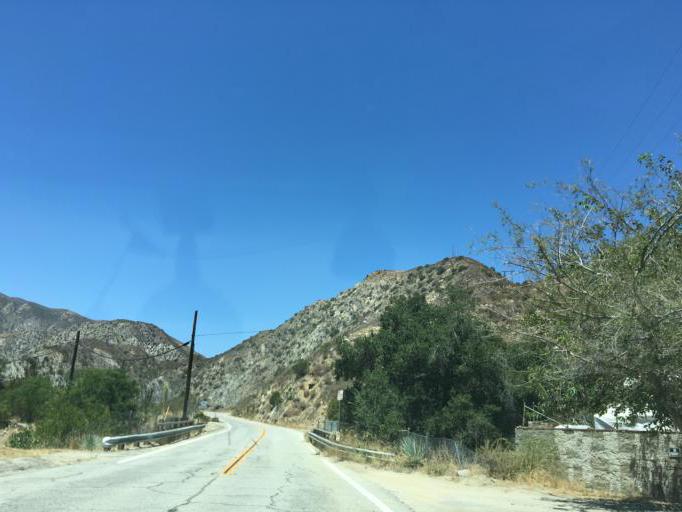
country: US
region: California
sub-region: Los Angeles County
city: La Crescenta-Montrose
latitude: 34.3028
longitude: -118.2558
